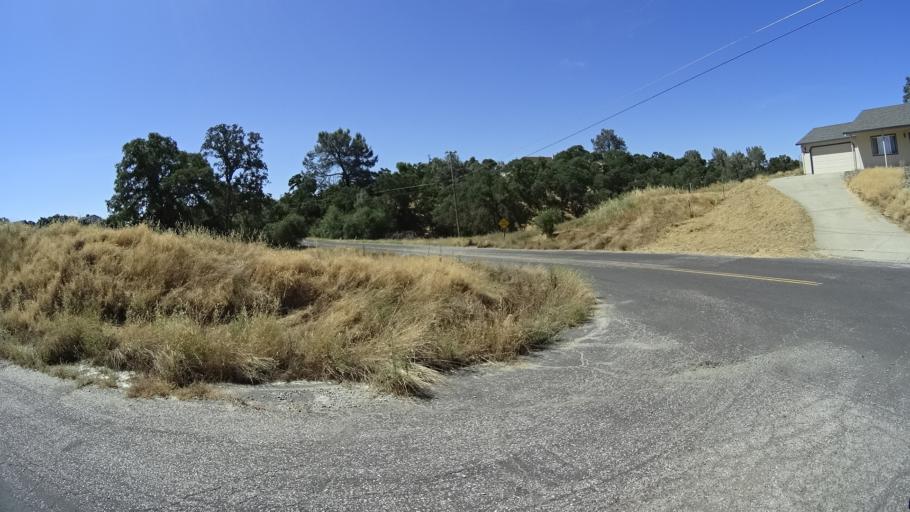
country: US
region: California
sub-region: Calaveras County
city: Valley Springs
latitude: 38.1579
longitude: -120.8336
